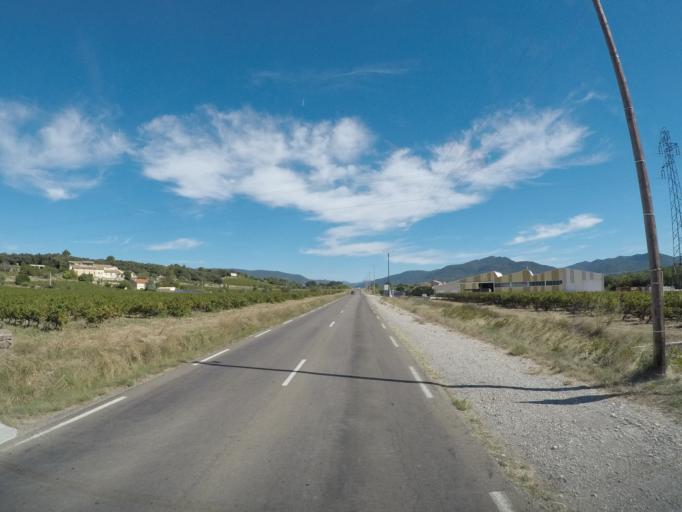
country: FR
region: Rhone-Alpes
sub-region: Departement de la Drome
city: Vinsobres
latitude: 44.3158
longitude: 5.0552
